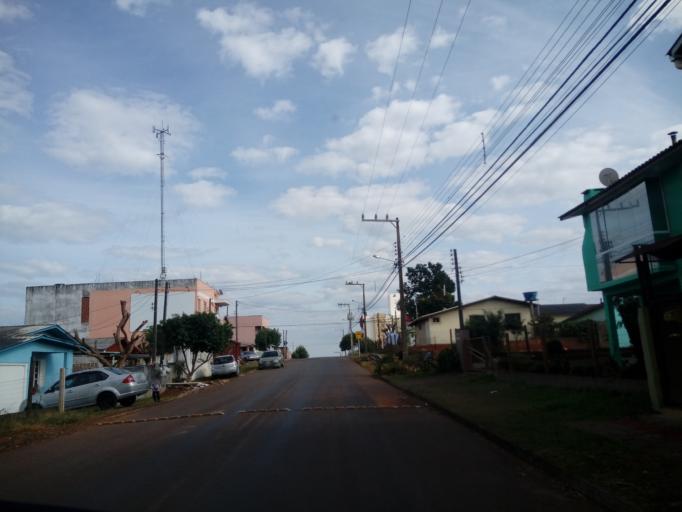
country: BR
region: Santa Catarina
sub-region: Chapeco
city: Chapeco
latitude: -27.1216
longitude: -52.6249
